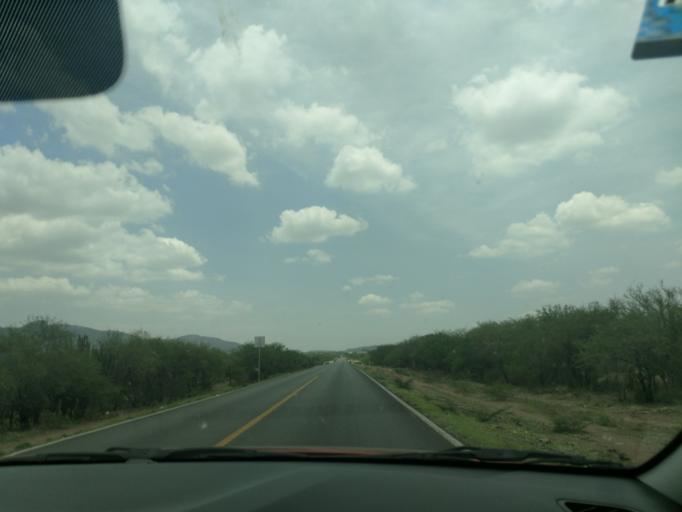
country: MX
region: San Luis Potosi
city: Villa Juarez
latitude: 22.0187
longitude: -100.3960
